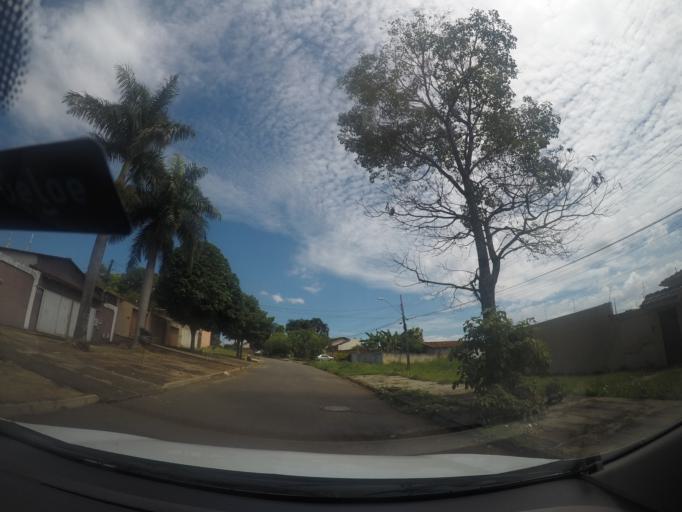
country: BR
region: Goias
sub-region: Goiania
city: Goiania
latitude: -16.6617
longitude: -49.3367
